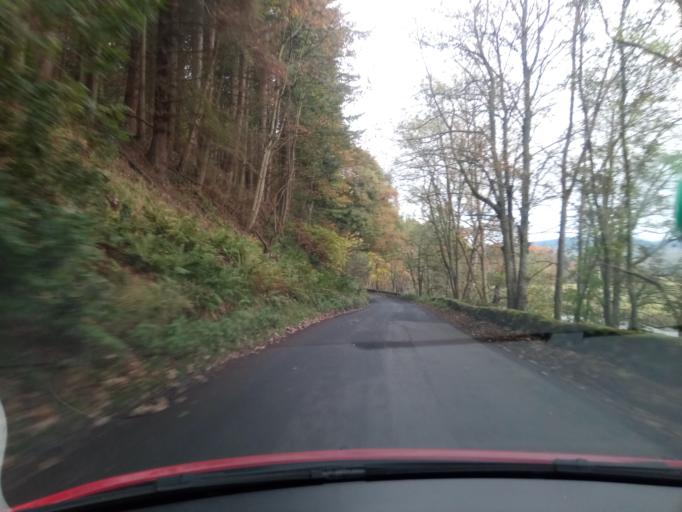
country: GB
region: Scotland
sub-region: The Scottish Borders
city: Innerleithen
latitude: 55.6240
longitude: -3.0993
